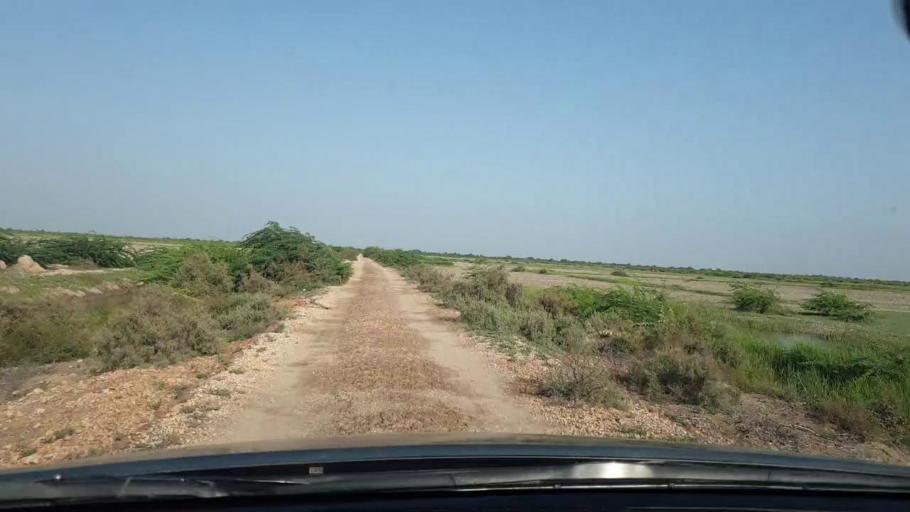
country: PK
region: Sindh
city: Naukot
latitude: 24.8336
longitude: 69.2456
